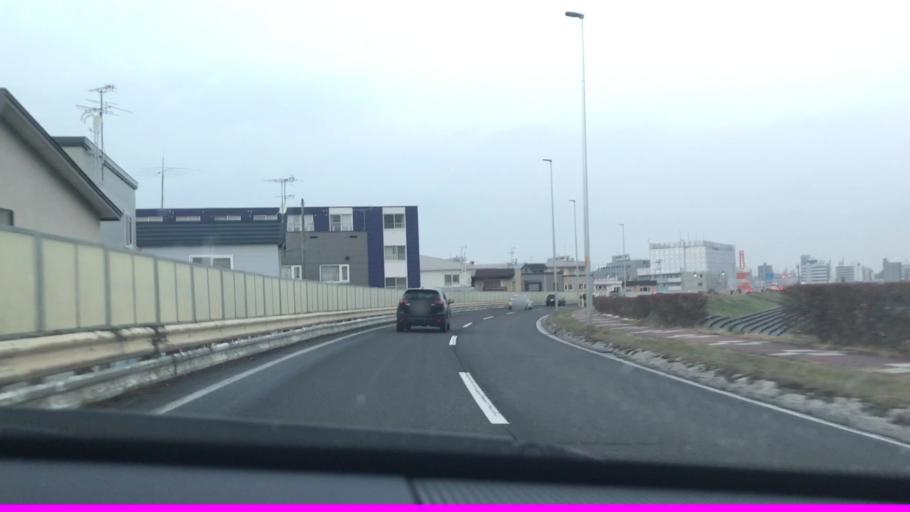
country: JP
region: Hokkaido
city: Sapporo
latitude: 43.0267
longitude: 141.3513
